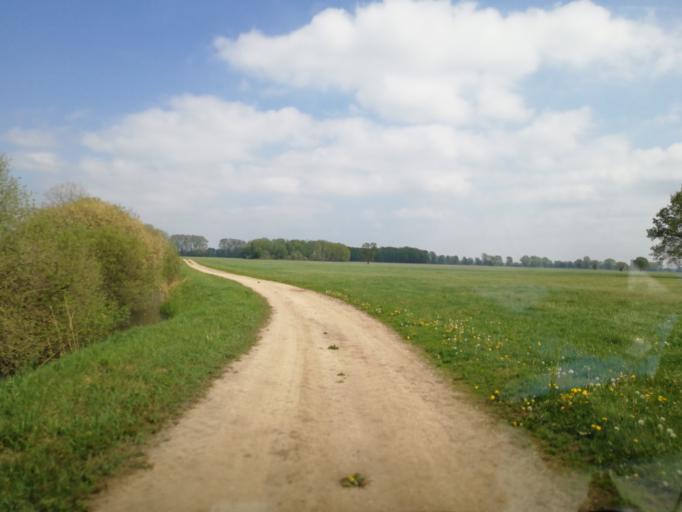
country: DE
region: Brandenburg
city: Doberlug-Kirchhain
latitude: 51.6747
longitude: 13.5462
